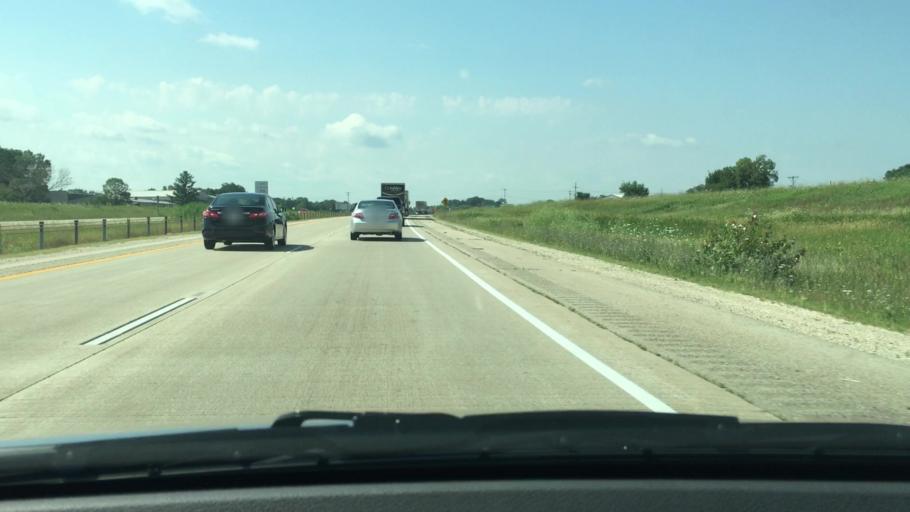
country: US
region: Wisconsin
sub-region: Fond du Lac County
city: Fond du Lac
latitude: 43.7591
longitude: -88.4752
